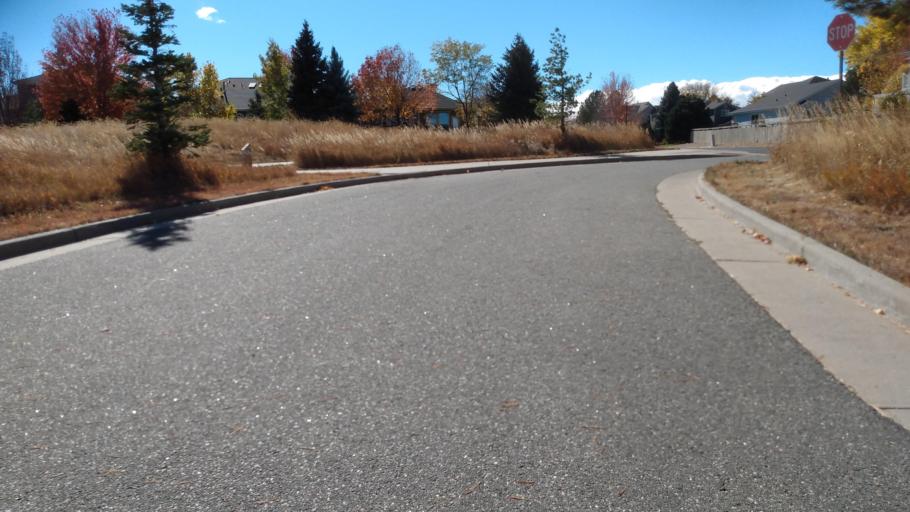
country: US
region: Colorado
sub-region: Boulder County
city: Lafayette
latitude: 39.9701
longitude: -105.0951
